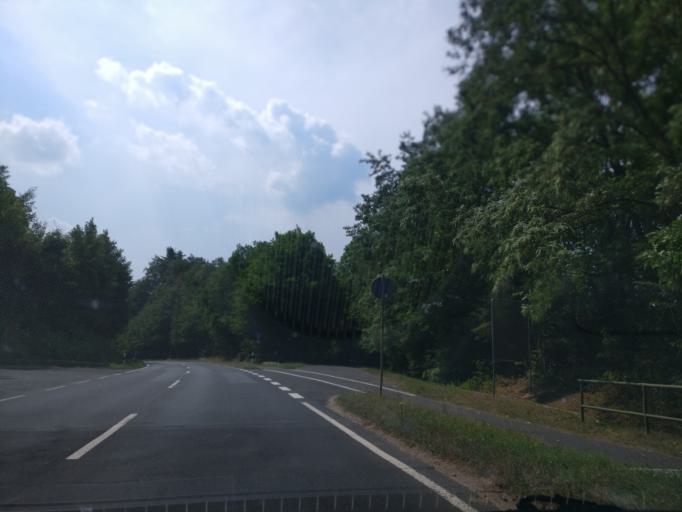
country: DE
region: Lower Saxony
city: Hannoversch Munden
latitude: 51.4548
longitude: 9.6413
